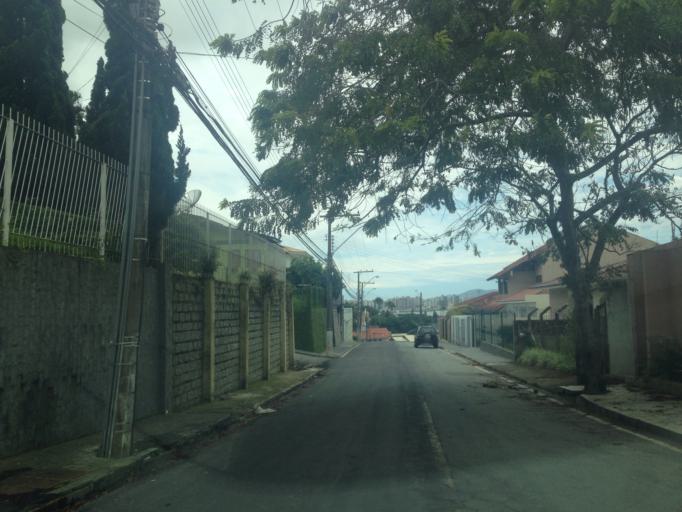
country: BR
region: Santa Catarina
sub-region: Sao Jose
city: Campinas
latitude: -27.6199
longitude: -48.6316
